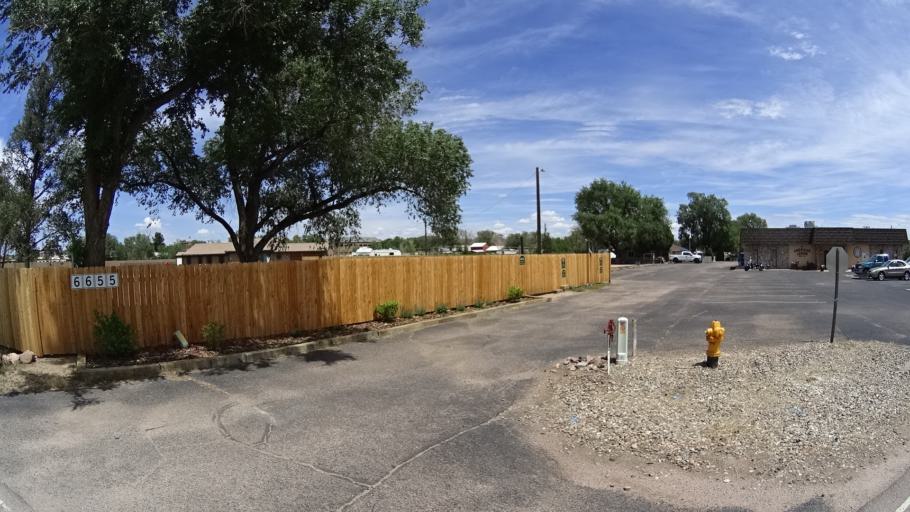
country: US
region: Colorado
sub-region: El Paso County
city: Security-Widefield
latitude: 38.7348
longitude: -104.7337
